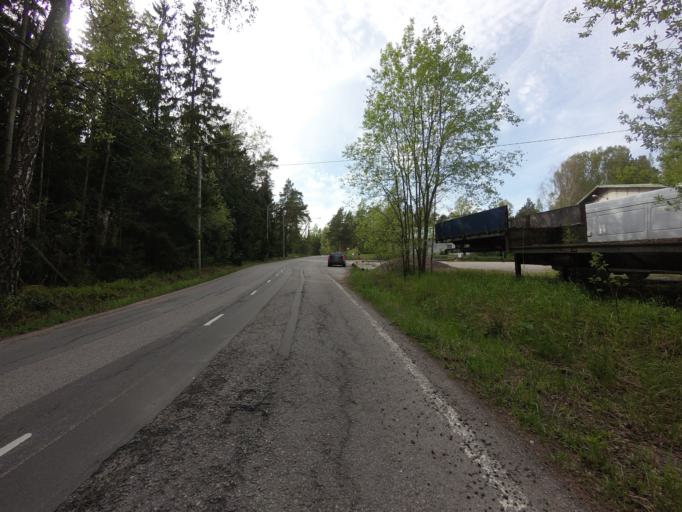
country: FI
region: Uusimaa
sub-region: Helsinki
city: Koukkuniemi
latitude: 60.1142
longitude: 24.7016
